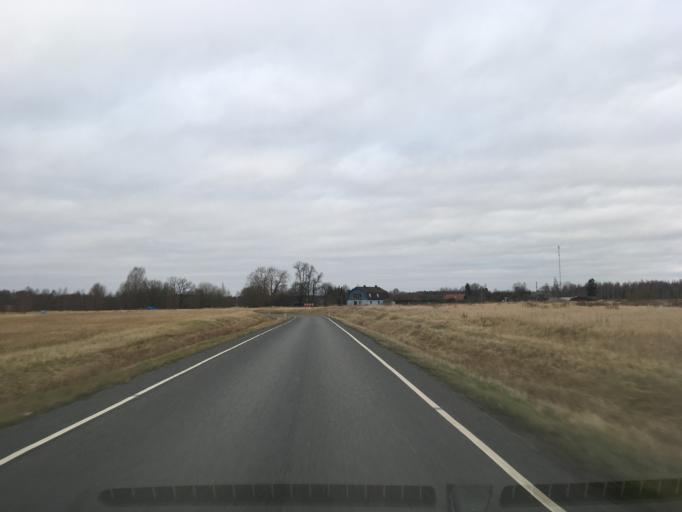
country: EE
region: Paernumaa
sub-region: Audru vald
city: Audru
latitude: 58.4136
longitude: 24.3734
